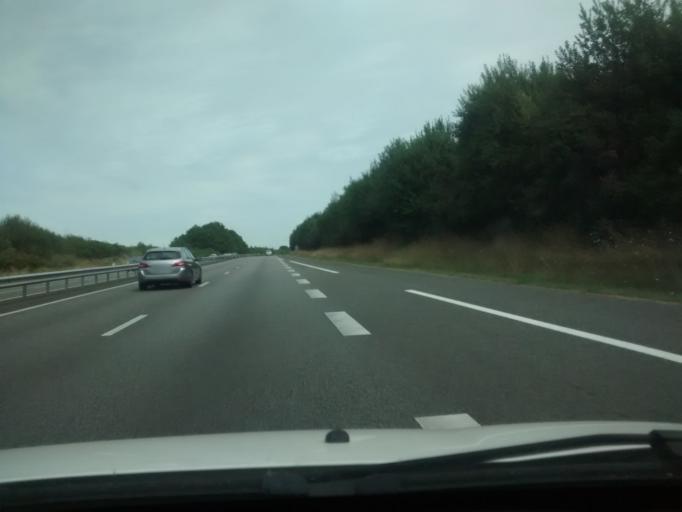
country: FR
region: Brittany
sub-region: Departement d'Ille-et-Vilaine
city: Liffre
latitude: 48.2073
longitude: -1.5240
